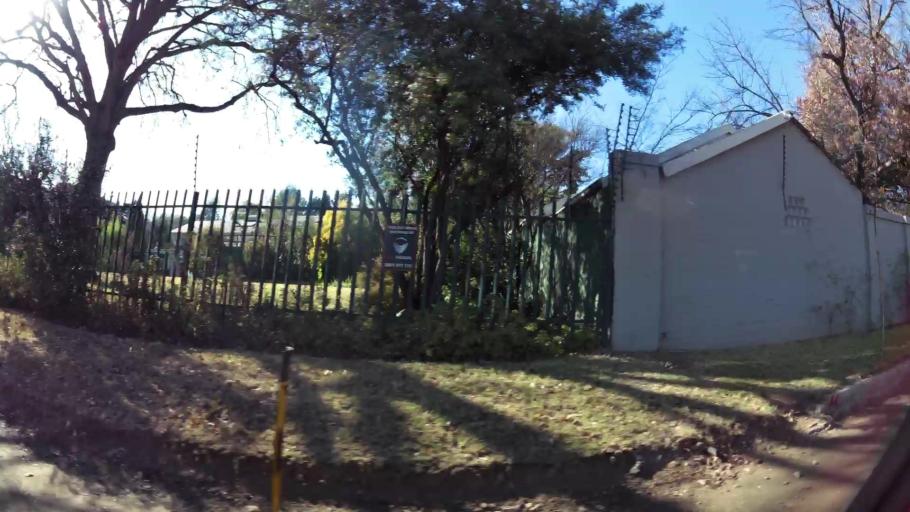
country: ZA
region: Gauteng
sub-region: City of Johannesburg Metropolitan Municipality
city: Johannesburg
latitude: -26.1237
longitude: 28.0171
